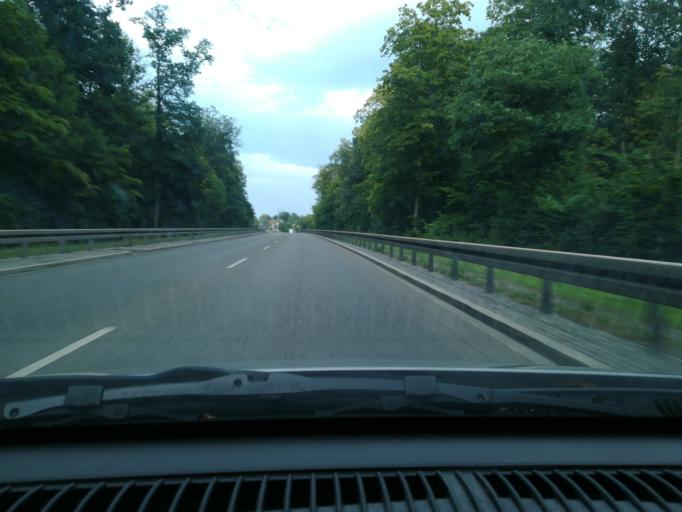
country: DE
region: Baden-Wuerttemberg
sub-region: Freiburg Region
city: Singen
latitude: 47.7502
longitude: 8.8329
